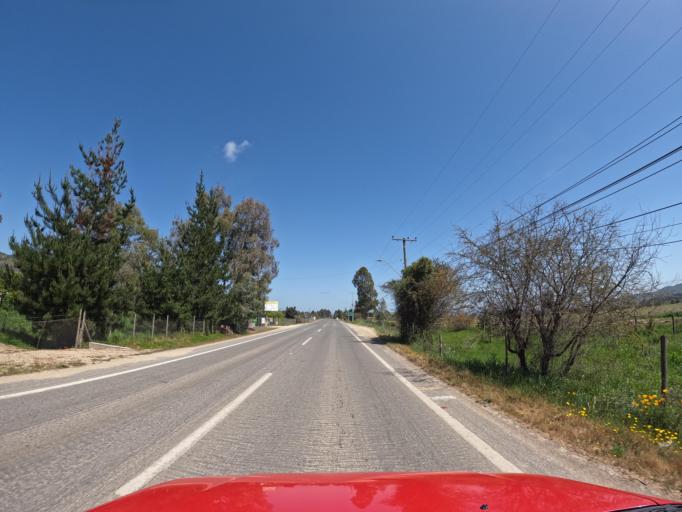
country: CL
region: O'Higgins
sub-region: Provincia de Colchagua
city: Santa Cruz
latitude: -34.7297
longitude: -71.6713
